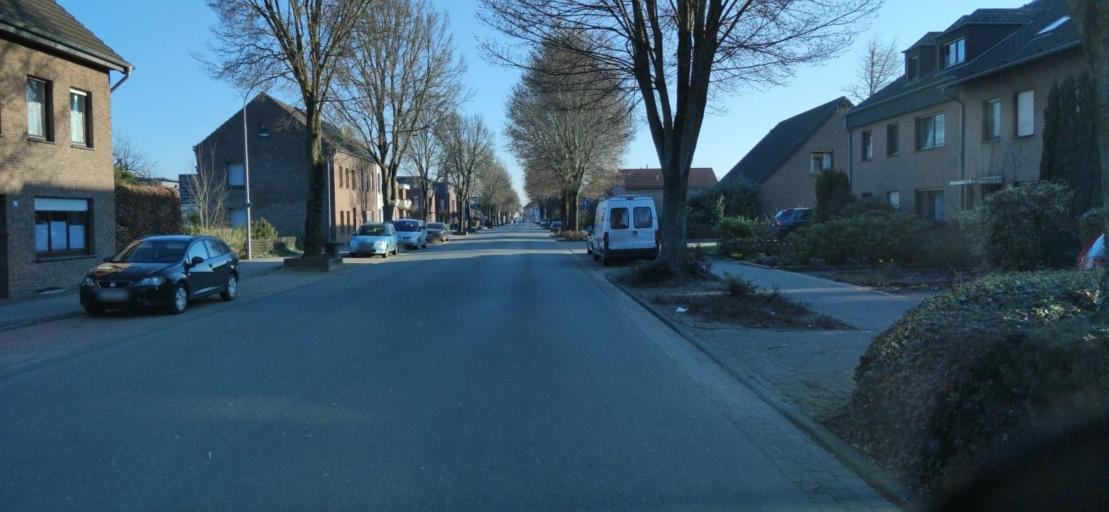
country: DE
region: North Rhine-Westphalia
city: Straelen
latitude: 51.4399
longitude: 6.2624
